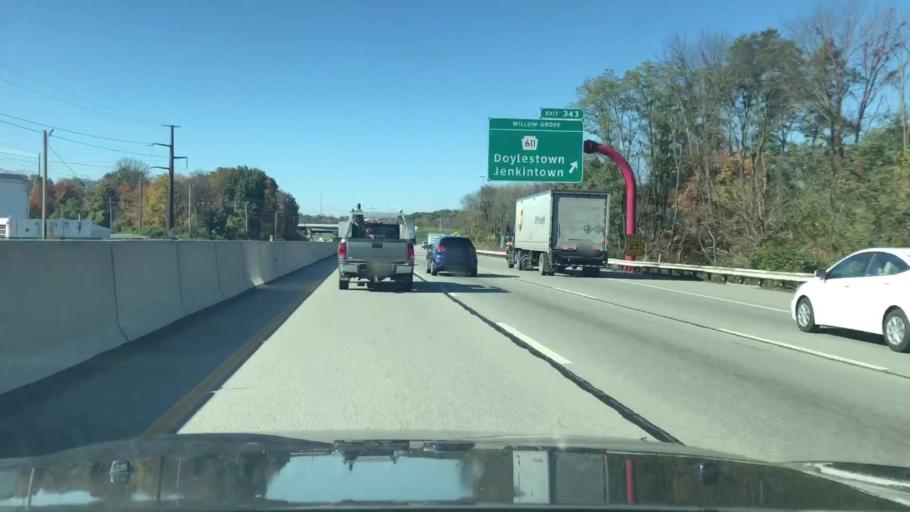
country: US
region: Pennsylvania
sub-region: Montgomery County
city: Hatboro
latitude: 40.1626
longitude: -75.1142
